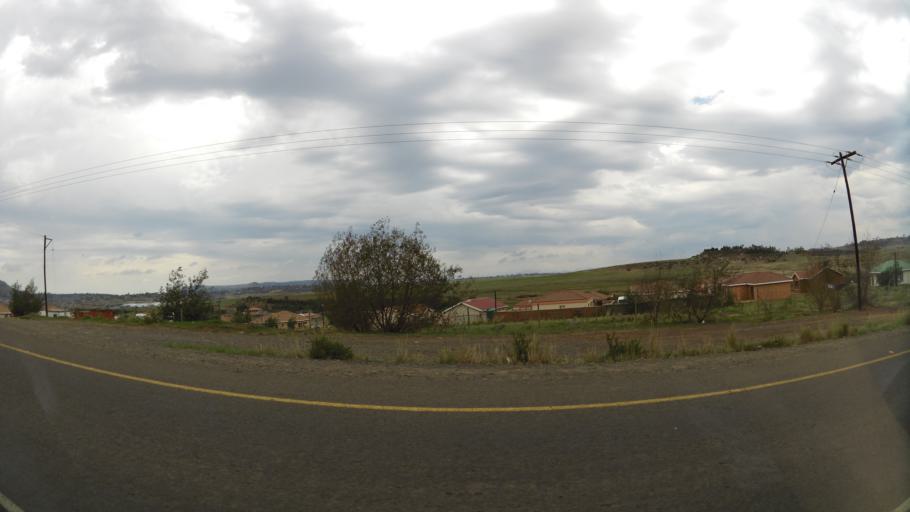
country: LS
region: Maseru
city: Maseru
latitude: -29.3942
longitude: 27.4748
